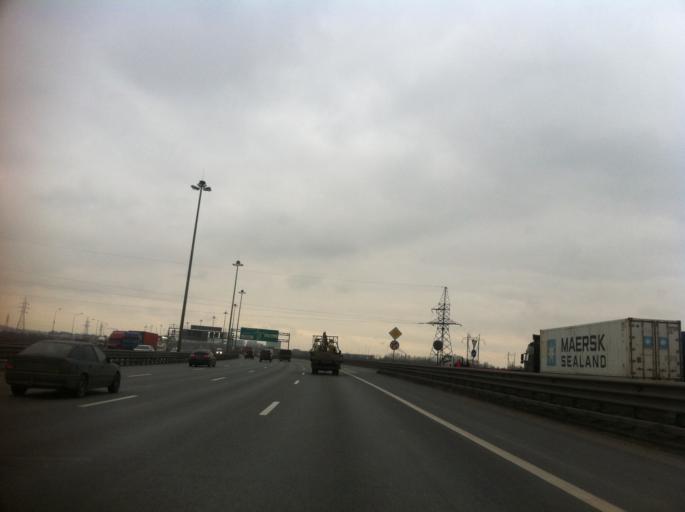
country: RU
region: St.-Petersburg
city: Shushary
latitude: 59.8149
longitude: 30.3545
